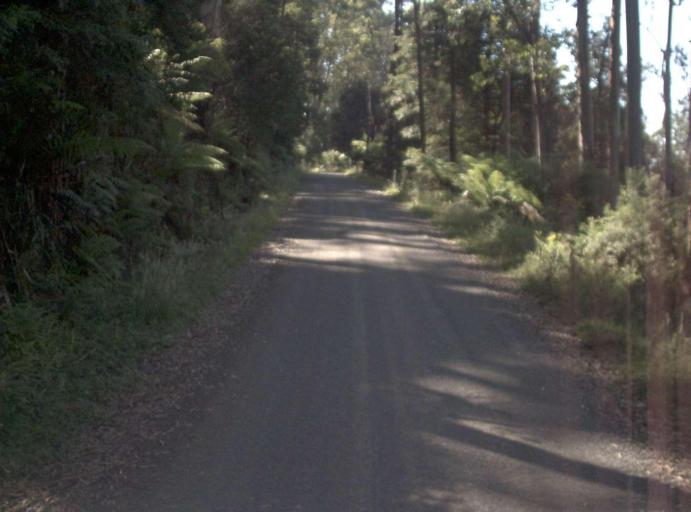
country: AU
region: Victoria
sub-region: Yarra Ranges
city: Millgrove
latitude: -37.7160
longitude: 145.6239
